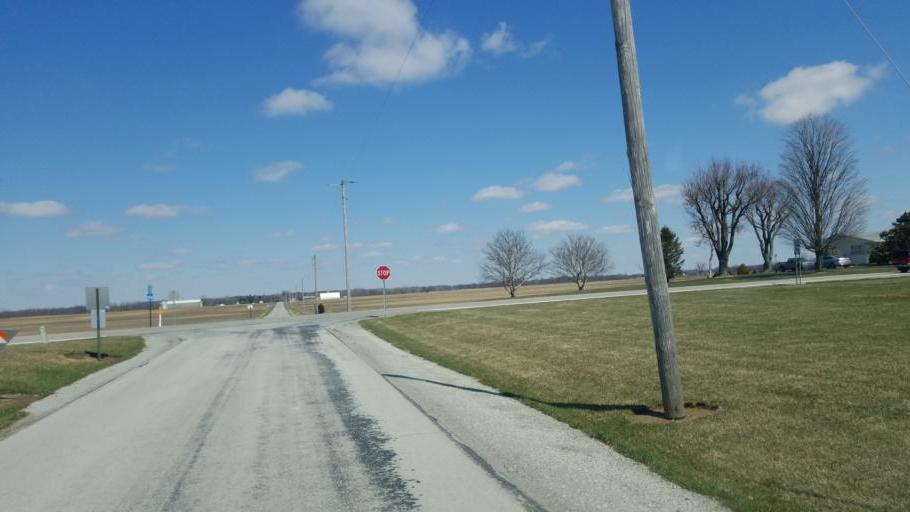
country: US
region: Ohio
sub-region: Wyandot County
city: Upper Sandusky
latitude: 40.7401
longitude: -83.1883
